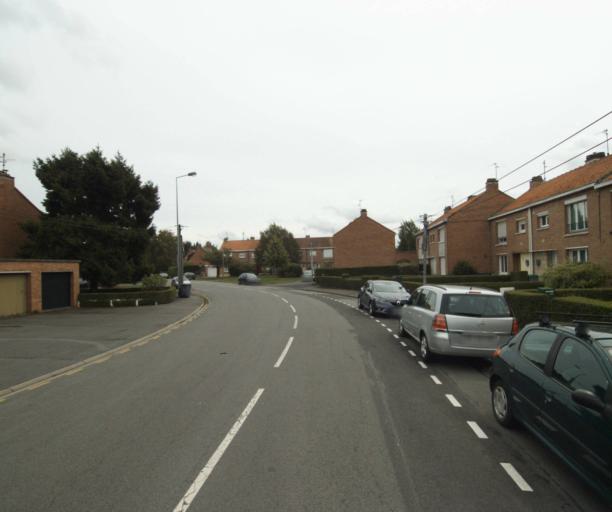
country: FR
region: Nord-Pas-de-Calais
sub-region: Departement du Nord
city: Faches-Thumesnil
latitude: 50.5943
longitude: 3.0711
